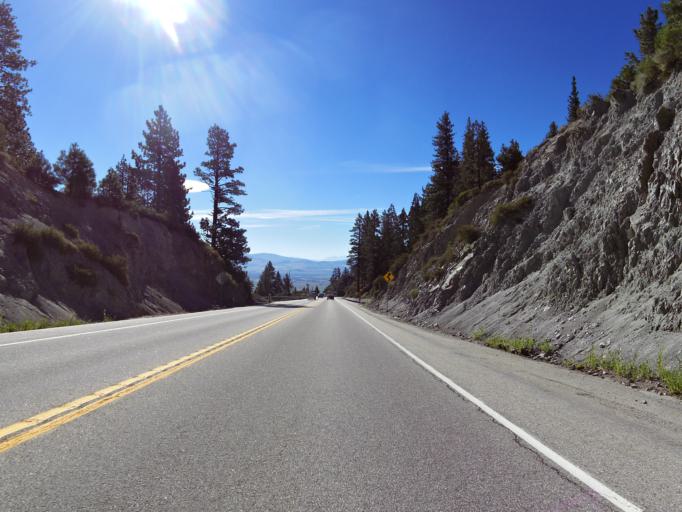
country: US
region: Nevada
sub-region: Douglas County
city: Kingsbury
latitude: 38.9754
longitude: -119.8595
